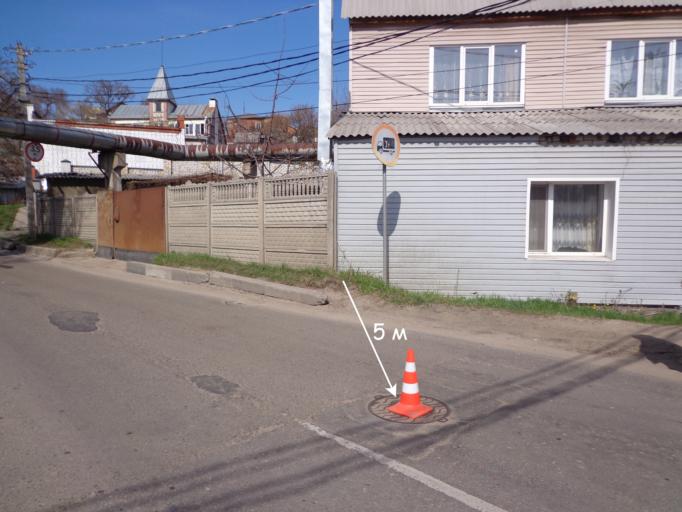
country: RU
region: Voronezj
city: Voronezh
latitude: 51.6613
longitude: 39.2168
